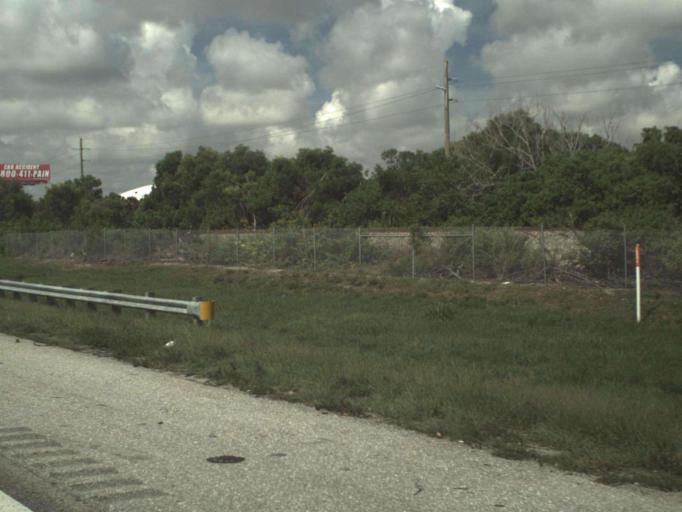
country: US
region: Florida
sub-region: Palm Beach County
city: Delray Beach
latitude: 26.4810
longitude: -80.0858
